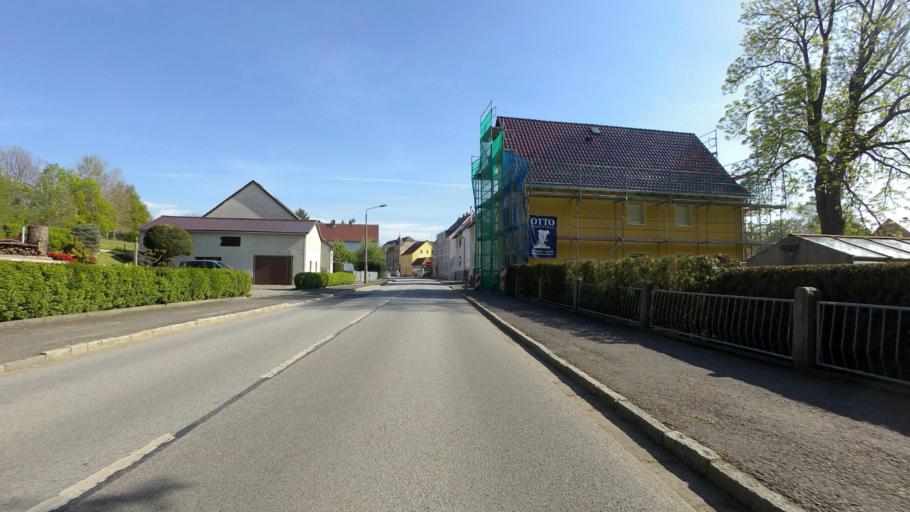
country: DE
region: Saxony
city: Kamenz
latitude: 51.2608
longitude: 14.1143
